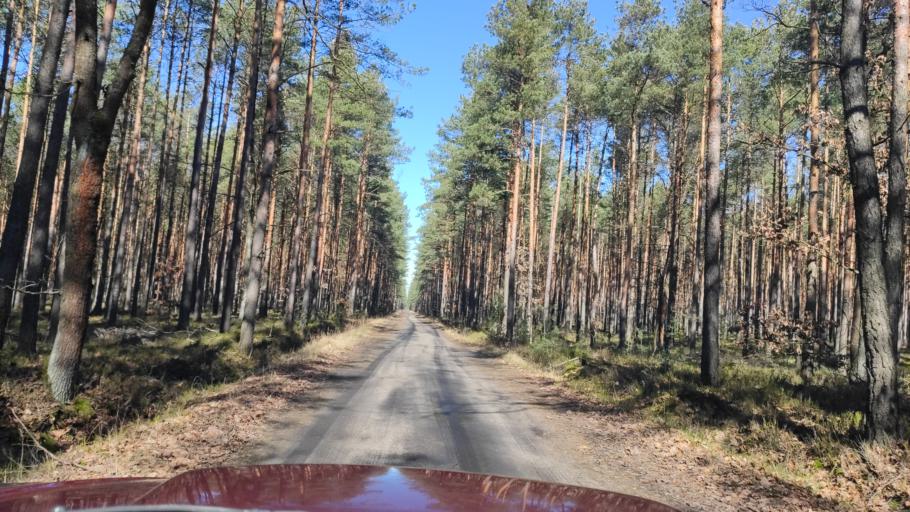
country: PL
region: Masovian Voivodeship
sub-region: Powiat zwolenski
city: Zwolen
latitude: 51.4195
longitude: 21.5530
